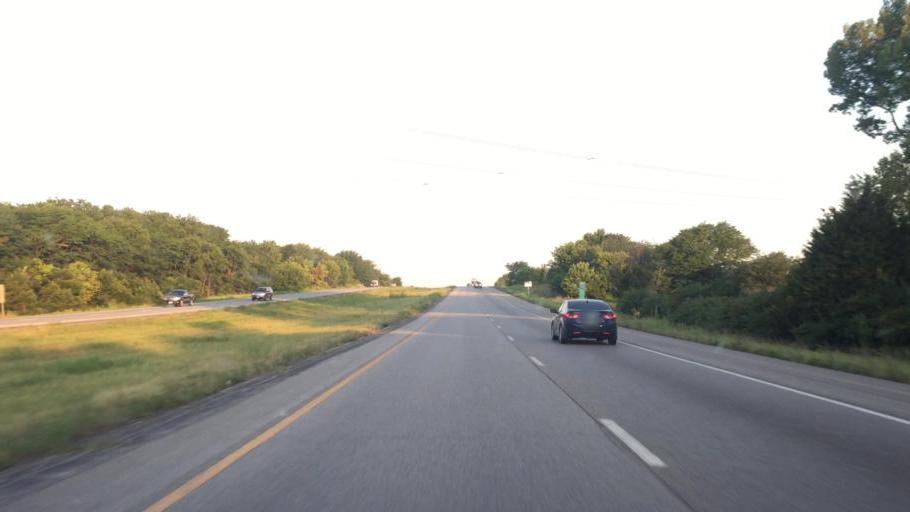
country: US
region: Missouri
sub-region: Clay County
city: Smithville
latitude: 39.3110
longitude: -94.5240
